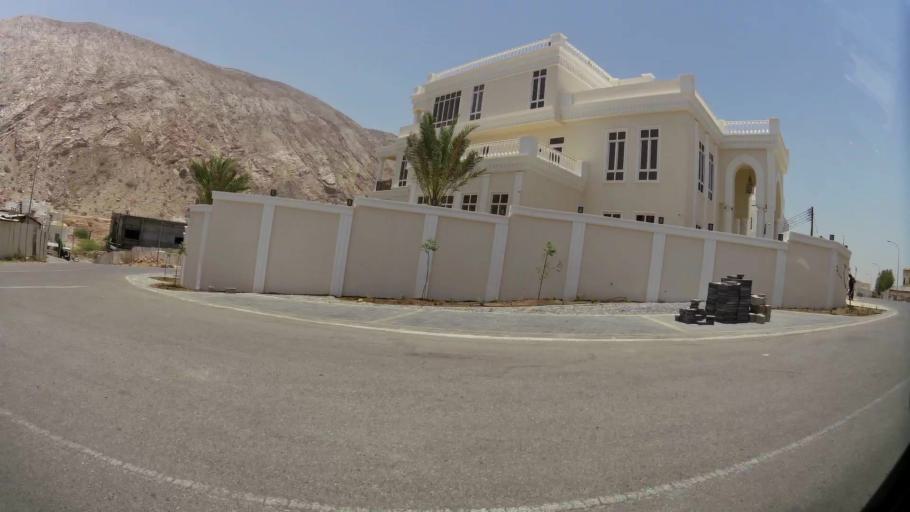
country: OM
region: Muhafazat Masqat
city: Bawshar
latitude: 23.5582
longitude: 58.4163
